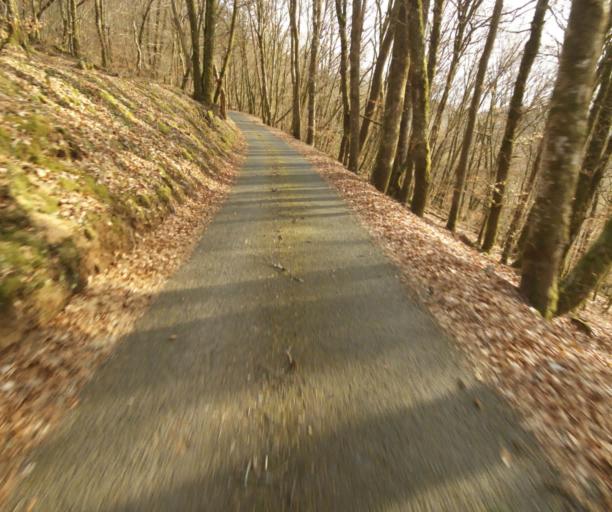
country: FR
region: Limousin
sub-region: Departement de la Correze
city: Correze
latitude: 45.3538
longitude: 1.8241
